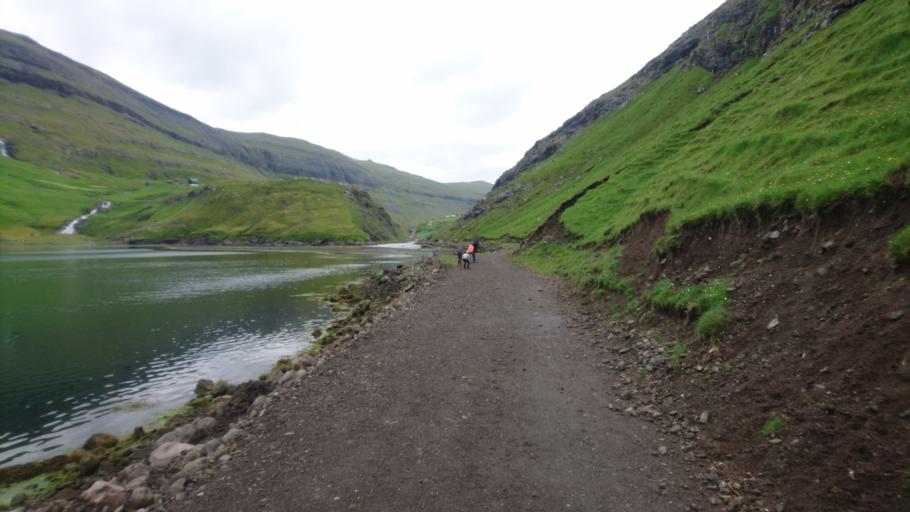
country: FO
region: Streymoy
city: Vestmanna
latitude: 62.2464
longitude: -7.1902
